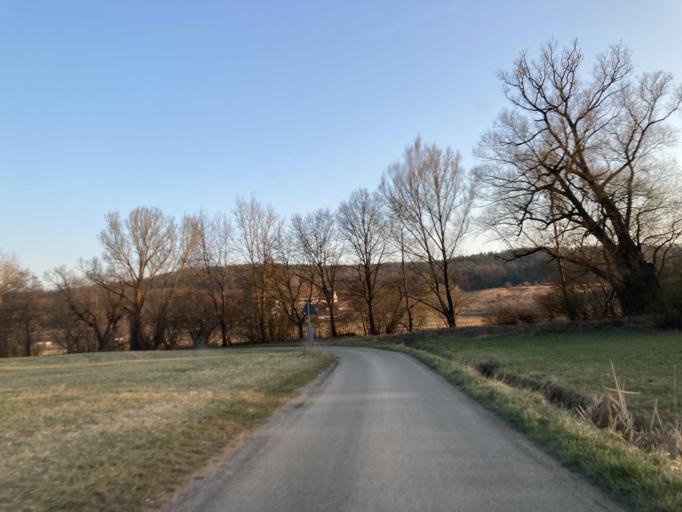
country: DE
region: Baden-Wuerttemberg
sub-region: Tuebingen Region
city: Tuebingen
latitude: 48.5207
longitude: 8.9990
